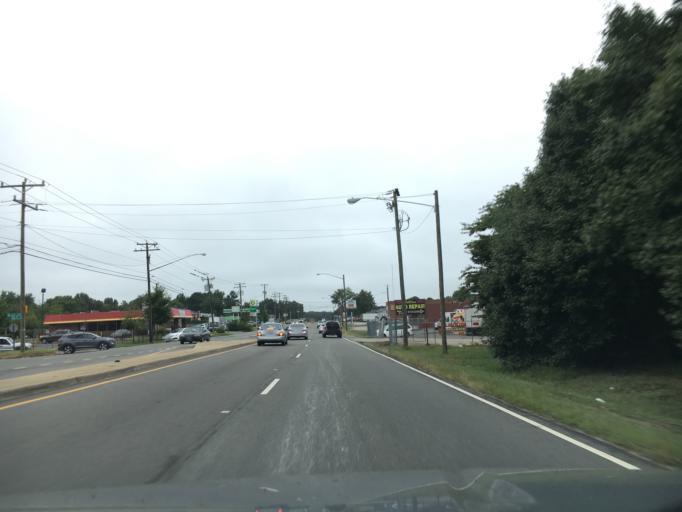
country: US
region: Virginia
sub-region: Chesterfield County
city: Bensley
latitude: 37.4873
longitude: -77.4958
